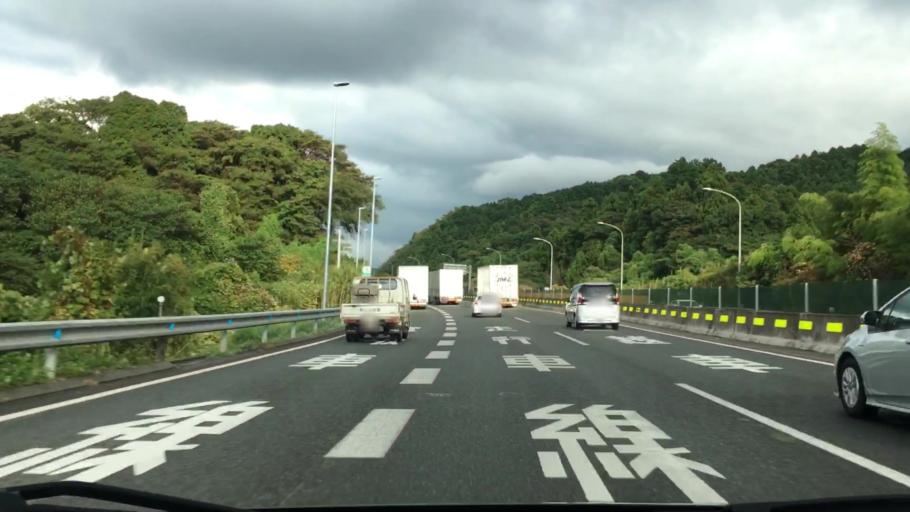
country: JP
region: Fukuoka
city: Nishifukuma
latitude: 33.7502
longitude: 130.5421
